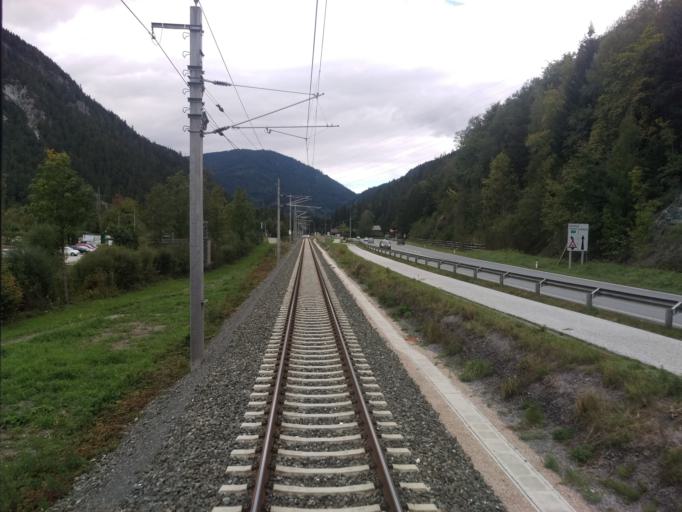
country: AT
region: Salzburg
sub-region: Politischer Bezirk Sankt Johann im Pongau
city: Forstau
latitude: 47.3893
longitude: 13.5984
